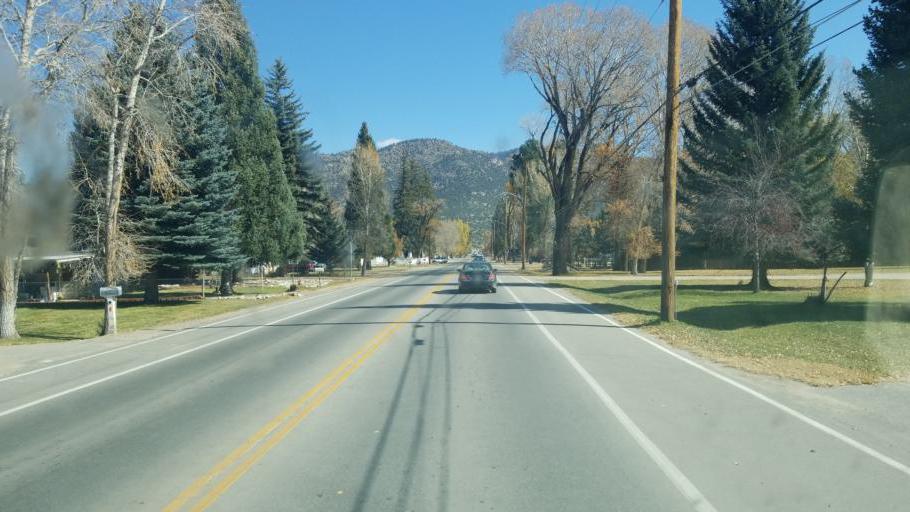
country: US
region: Colorado
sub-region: Chaffee County
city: Buena Vista
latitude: 38.8396
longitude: -106.1401
